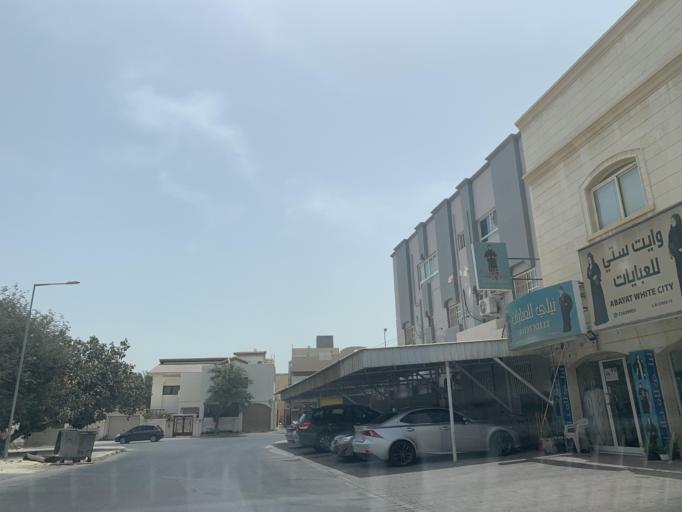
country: BH
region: Northern
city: Ar Rifa'
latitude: 26.1311
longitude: 50.5769
